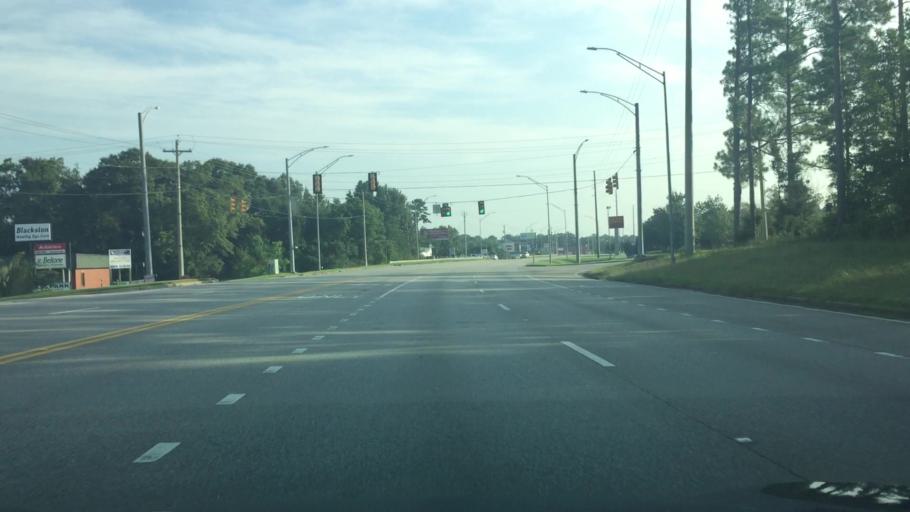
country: US
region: Alabama
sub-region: Covington County
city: Andalusia
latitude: 31.3130
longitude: -86.4994
